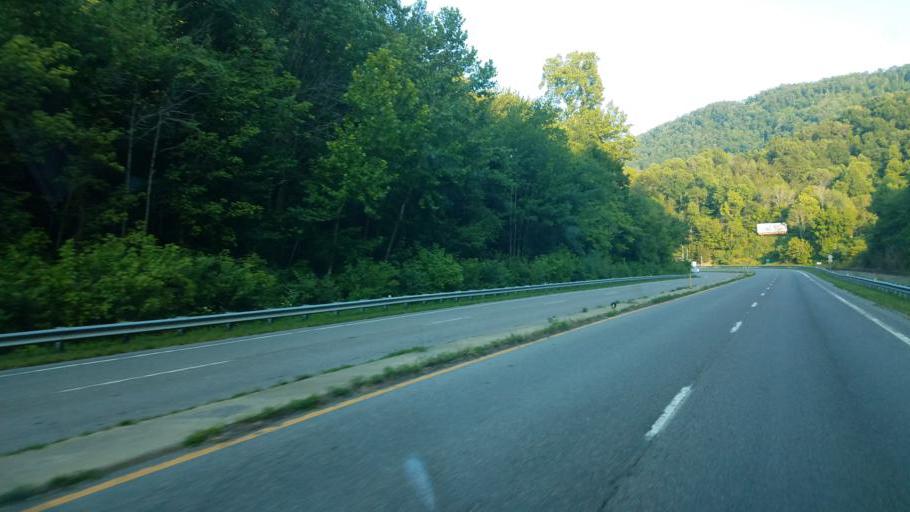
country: US
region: Tennessee
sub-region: Hawkins County
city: Church Hill
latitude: 36.6424
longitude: -82.7418
